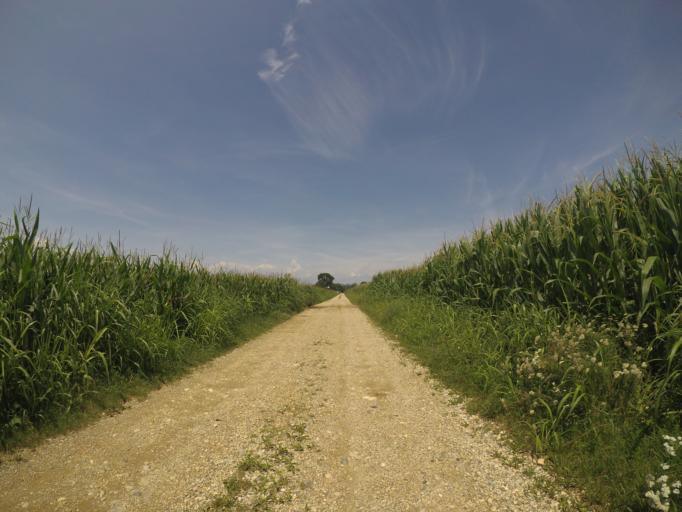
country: IT
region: Friuli Venezia Giulia
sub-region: Provincia di Udine
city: Lestizza
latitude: 45.9706
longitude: 13.0964
